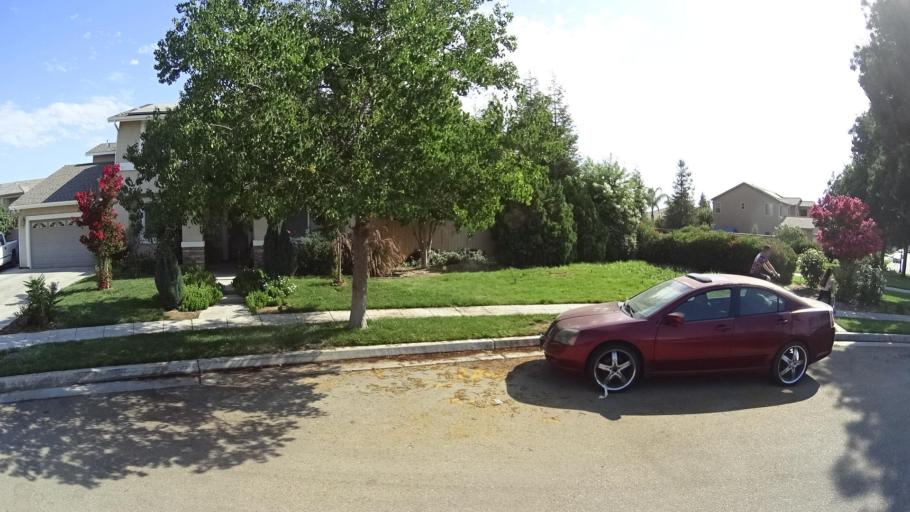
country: US
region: California
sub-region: Fresno County
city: Sunnyside
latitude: 36.7096
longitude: -119.6874
